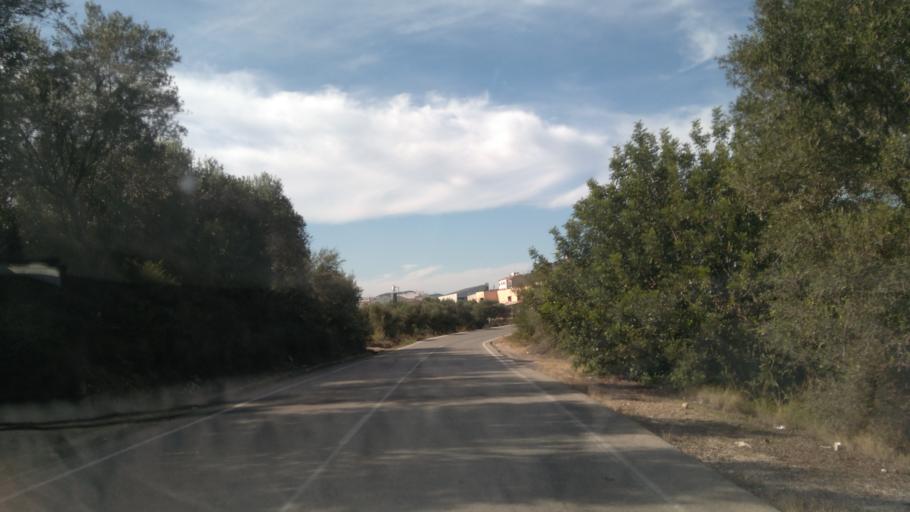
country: ES
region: Valencia
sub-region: Provincia de Valencia
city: Real de Montroi
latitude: 39.3319
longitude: -0.6038
